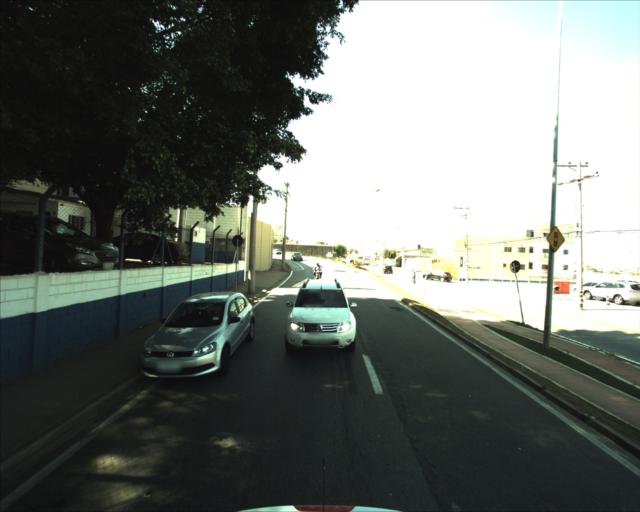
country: BR
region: Sao Paulo
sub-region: Sorocaba
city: Sorocaba
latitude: -23.4859
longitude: -47.4835
